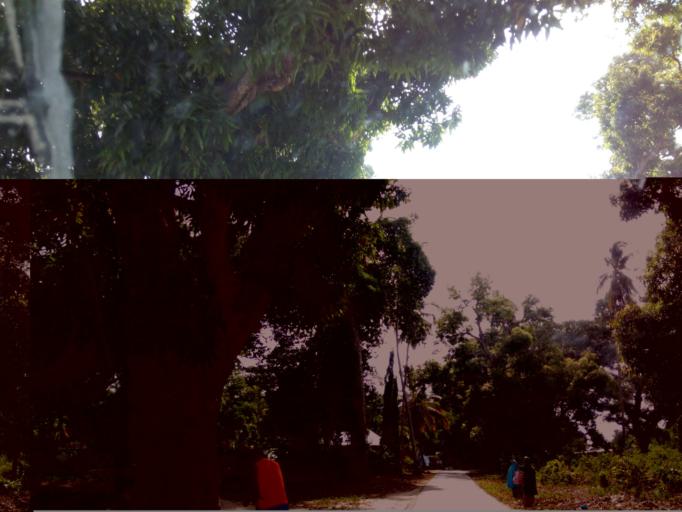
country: TZ
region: Zanzibar Central/South
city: Mahonda
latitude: -6.3091
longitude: 39.3759
